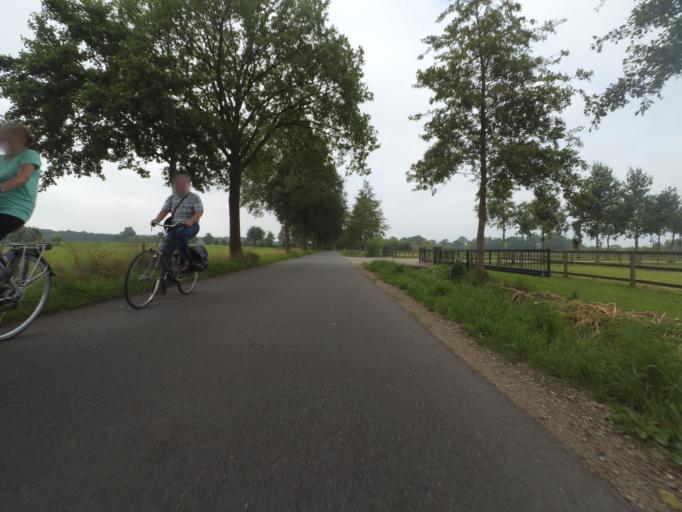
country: NL
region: Gelderland
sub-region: Gemeente Barneveld
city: Kootwijkerbroek
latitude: 52.1155
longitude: 5.6543
